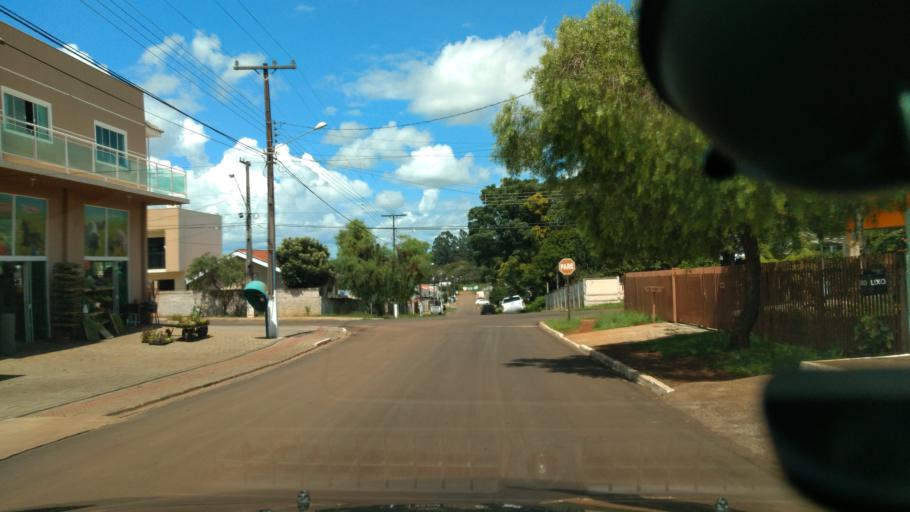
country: BR
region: Parana
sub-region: Guarapuava
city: Guarapuava
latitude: -25.3980
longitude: -51.4980
